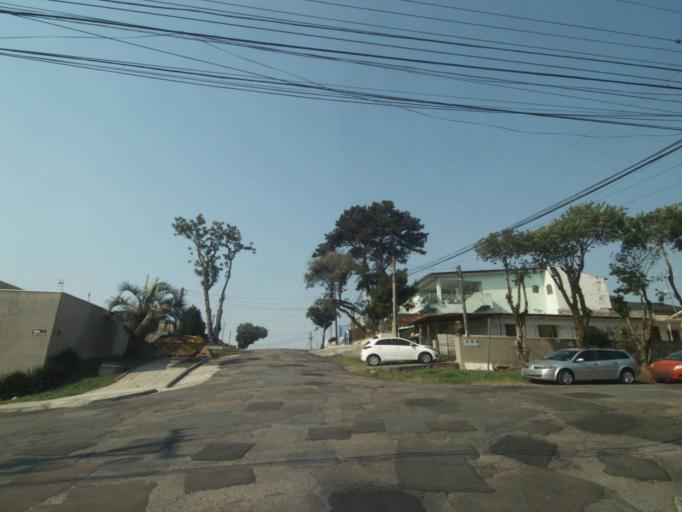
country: BR
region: Parana
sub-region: Sao Jose Dos Pinhais
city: Sao Jose dos Pinhais
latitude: -25.5030
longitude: -49.2778
